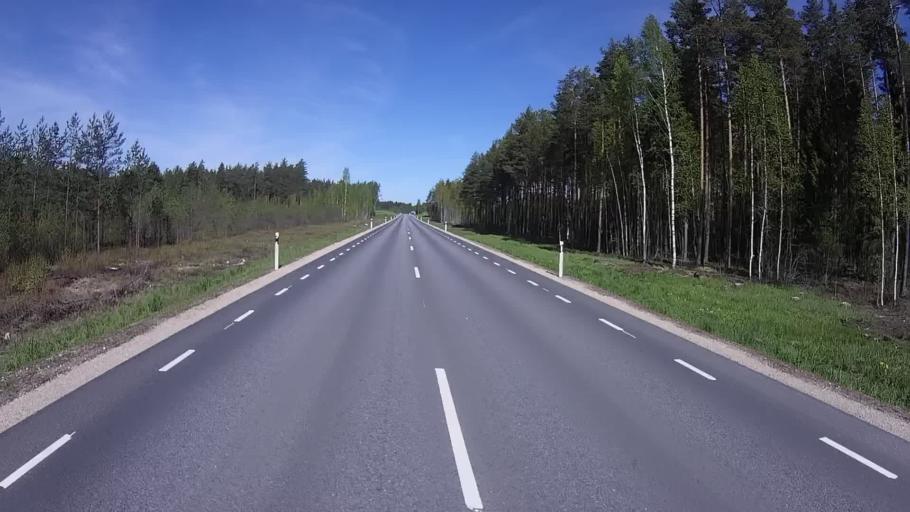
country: RU
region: Pskov
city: Pechory
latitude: 57.9709
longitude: 27.5880
